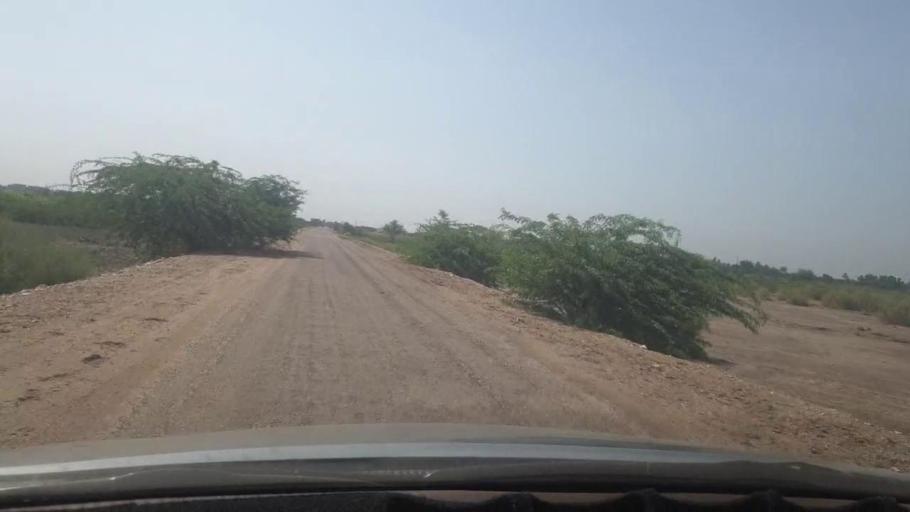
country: PK
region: Sindh
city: Ranipur
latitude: 27.2626
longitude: 68.5836
